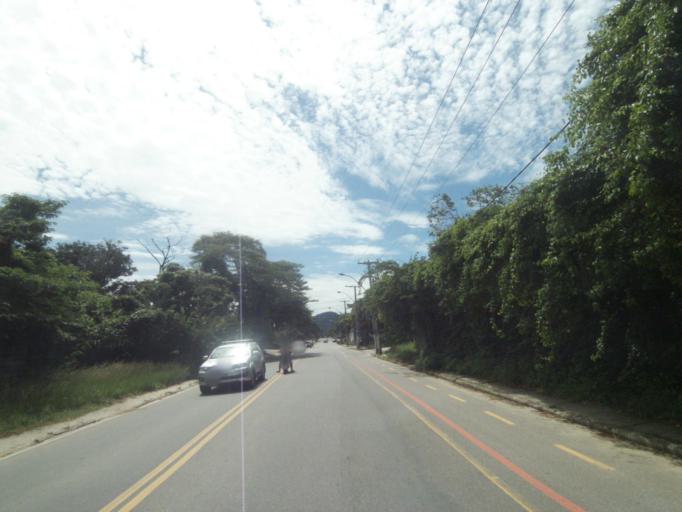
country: BR
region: Rio de Janeiro
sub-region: Niteroi
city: Niteroi
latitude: -22.9429
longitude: -43.0189
